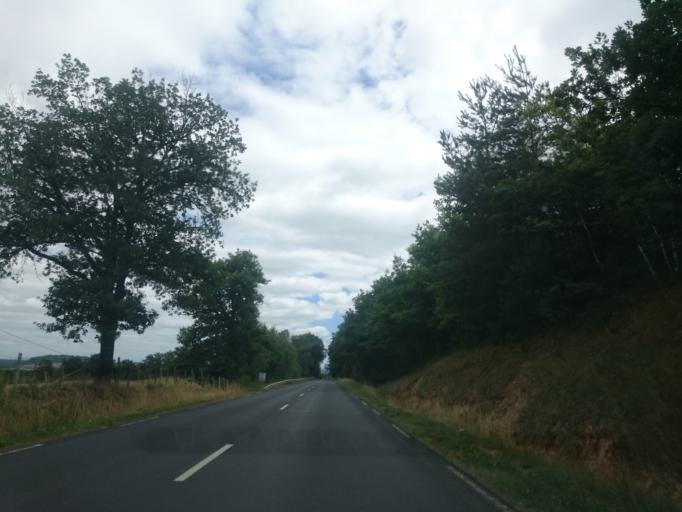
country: FR
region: Auvergne
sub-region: Departement du Cantal
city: Laroquebrou
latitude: 44.9661
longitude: 2.2459
